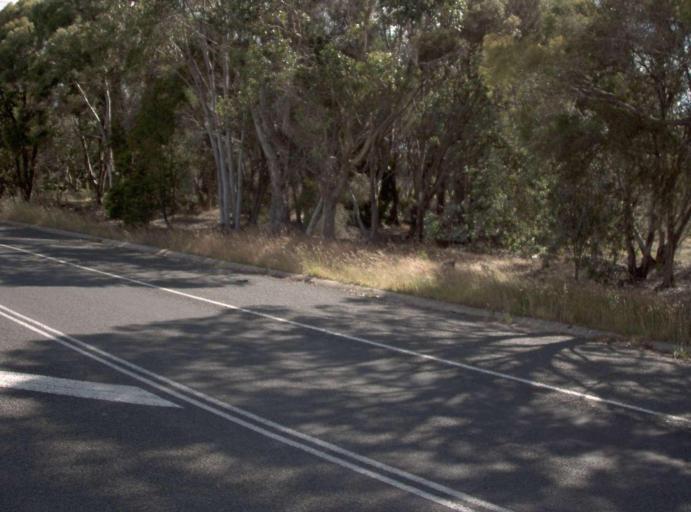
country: AU
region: Victoria
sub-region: Latrobe
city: Morwell
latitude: -38.2803
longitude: 146.4317
